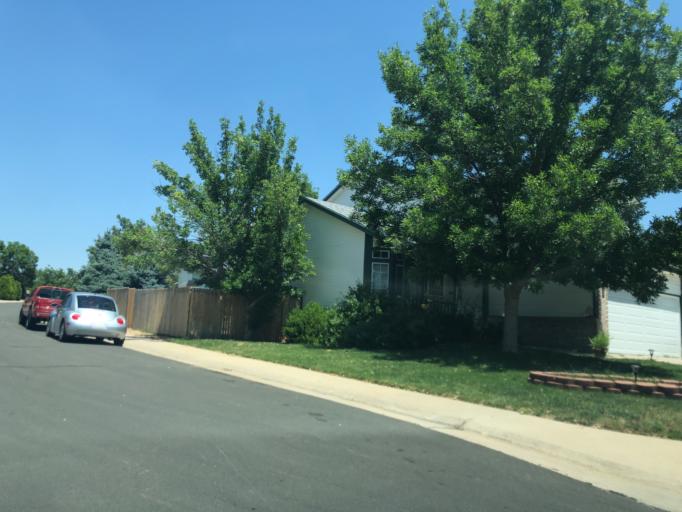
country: US
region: Colorado
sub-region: Arapahoe County
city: Dove Valley
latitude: 39.6263
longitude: -104.7732
